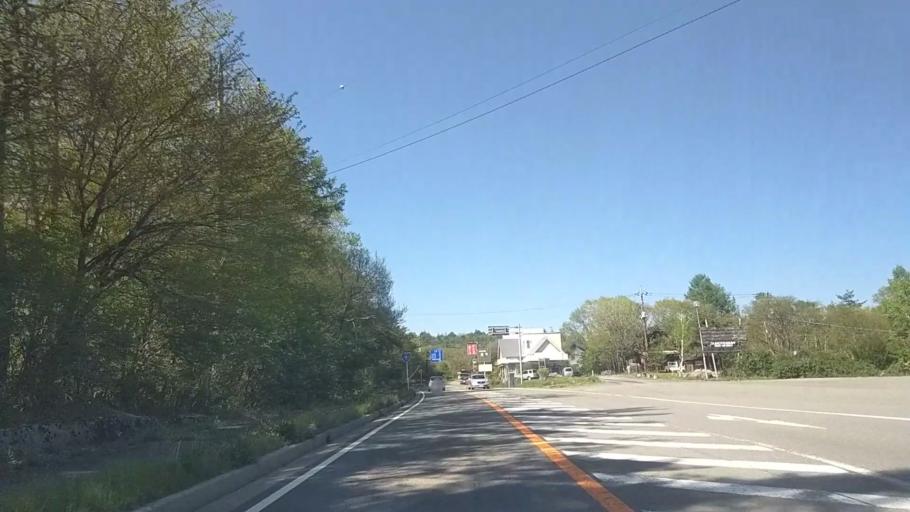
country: JP
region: Yamanashi
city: Nirasaki
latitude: 35.9282
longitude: 138.4425
